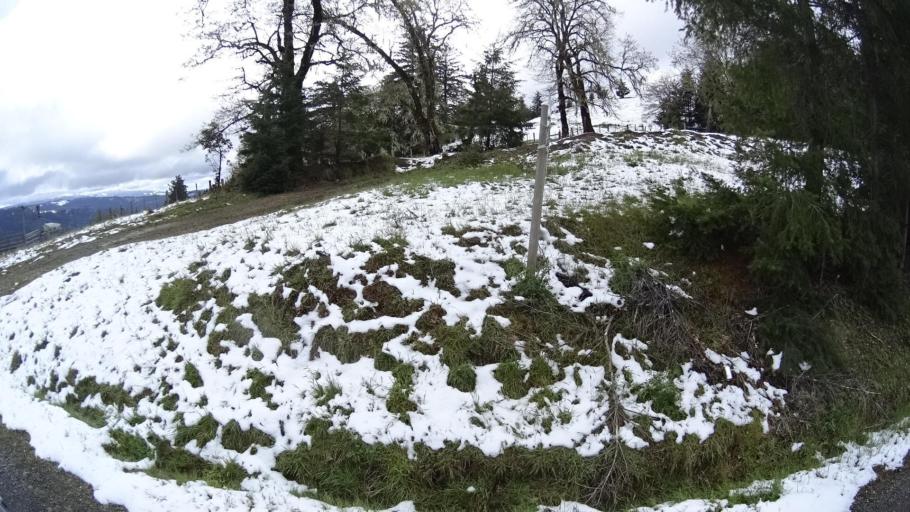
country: US
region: California
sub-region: Humboldt County
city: Blue Lake
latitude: 40.8806
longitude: -123.8714
